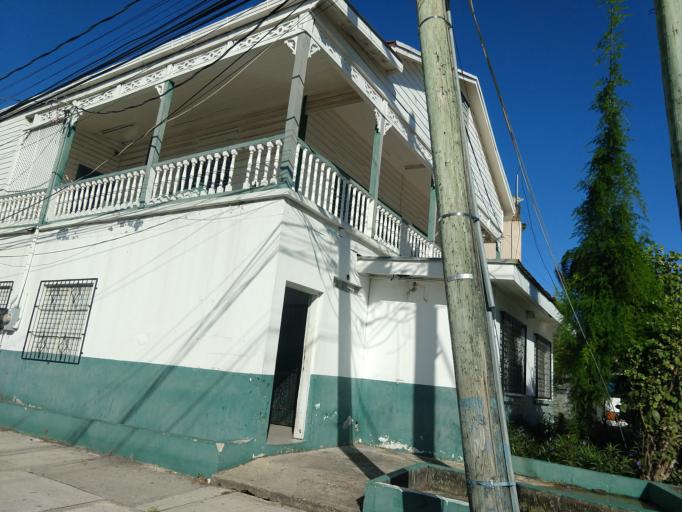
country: BZ
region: Belize
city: Belize City
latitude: 17.4959
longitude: -88.1845
